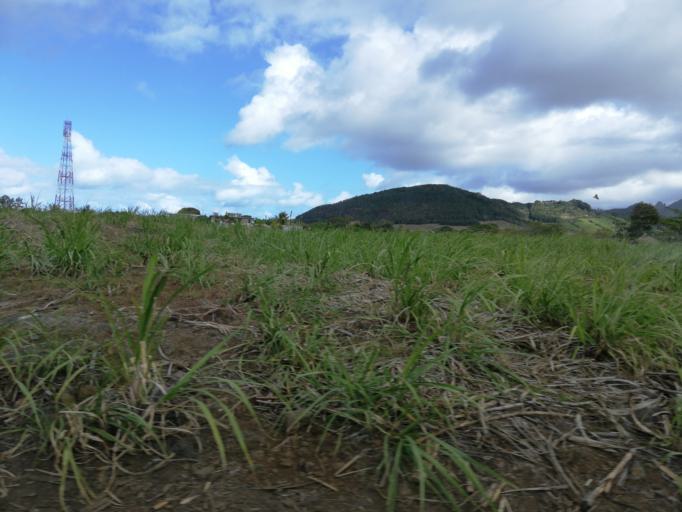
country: MU
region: Flacq
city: Grande Riviere Sud Est
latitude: -20.2731
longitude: 57.7703
